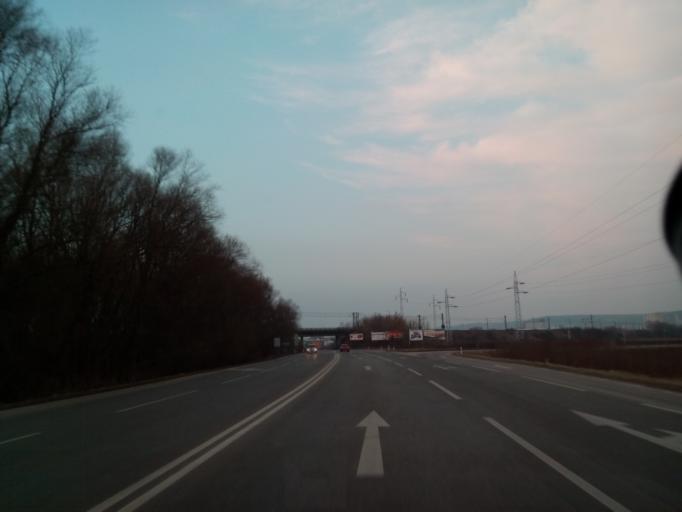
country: SK
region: Kosicky
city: Kosice
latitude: 48.6647
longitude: 21.2720
